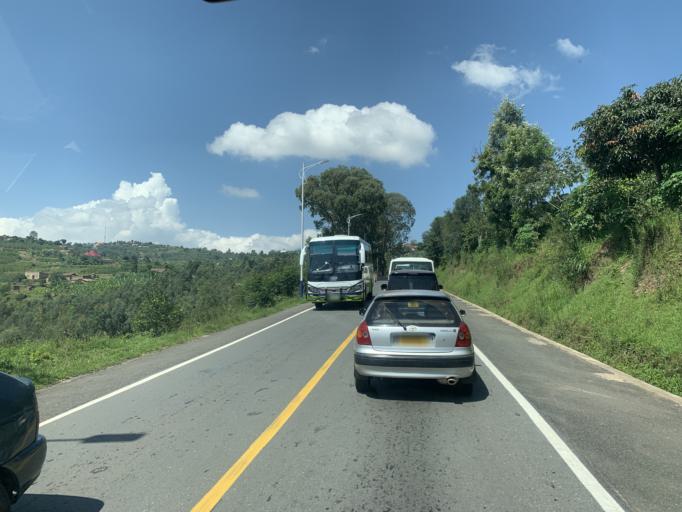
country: RW
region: Southern Province
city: Gitarama
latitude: -2.0570
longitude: 29.8052
